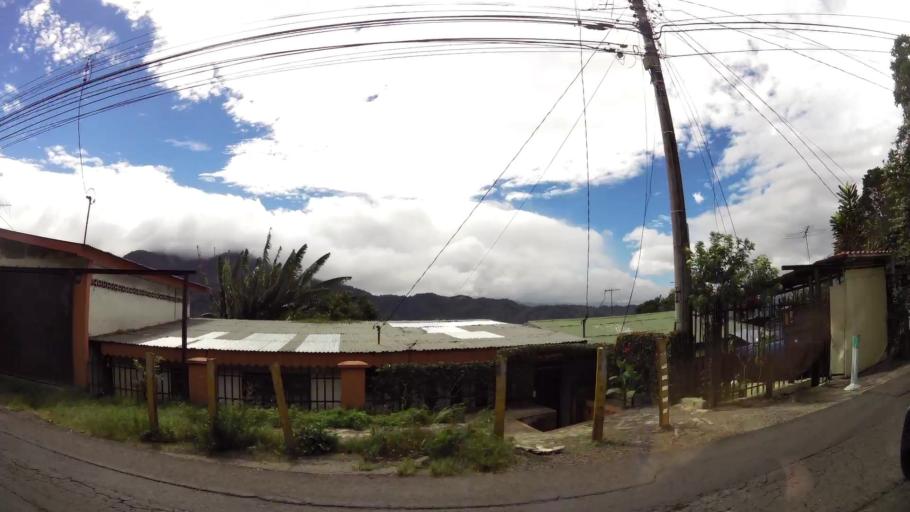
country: CR
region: Cartago
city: Tres Rios
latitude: 9.9113
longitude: -83.9881
